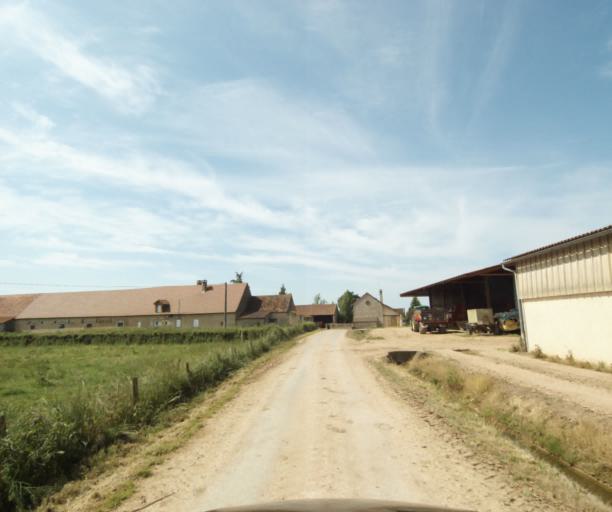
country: FR
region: Bourgogne
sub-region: Departement de Saone-et-Loire
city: Palinges
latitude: 46.5600
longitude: 4.1685
